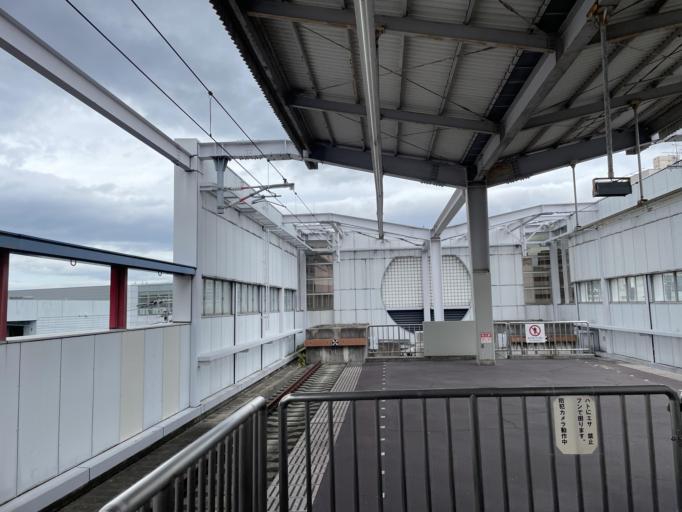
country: JP
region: Hyogo
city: Nishinomiya-hama
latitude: 34.7319
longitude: 135.3516
